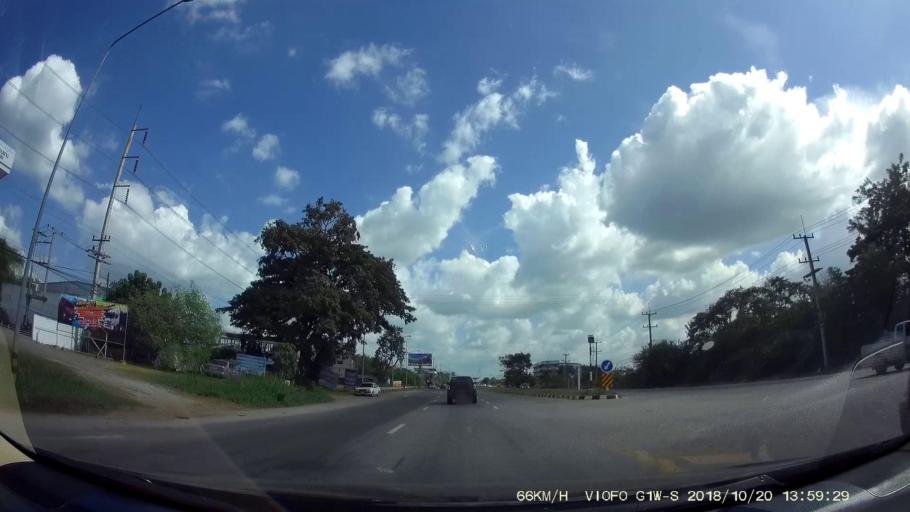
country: TH
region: Khon Kaen
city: Chum Phae
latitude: 16.5241
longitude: 102.1130
